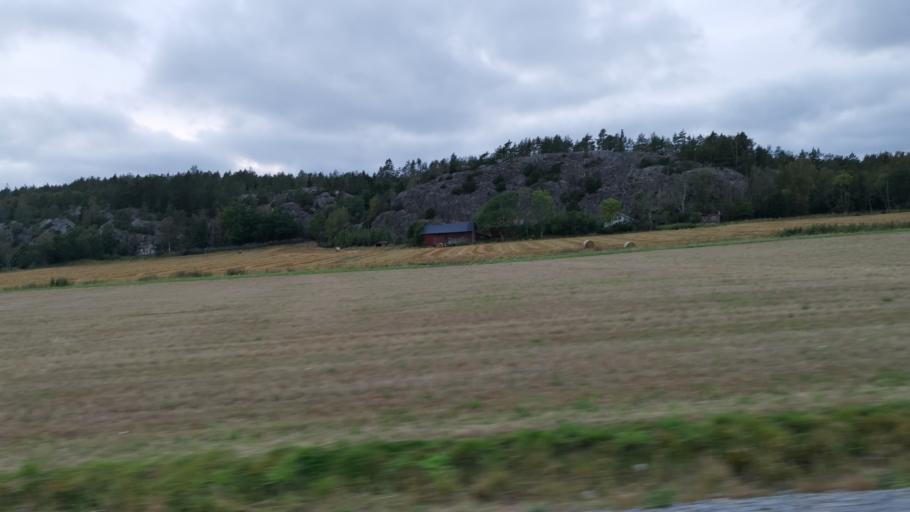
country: SE
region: Vaestra Goetaland
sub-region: Tanums Kommun
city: Tanumshede
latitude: 58.6481
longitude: 11.3393
